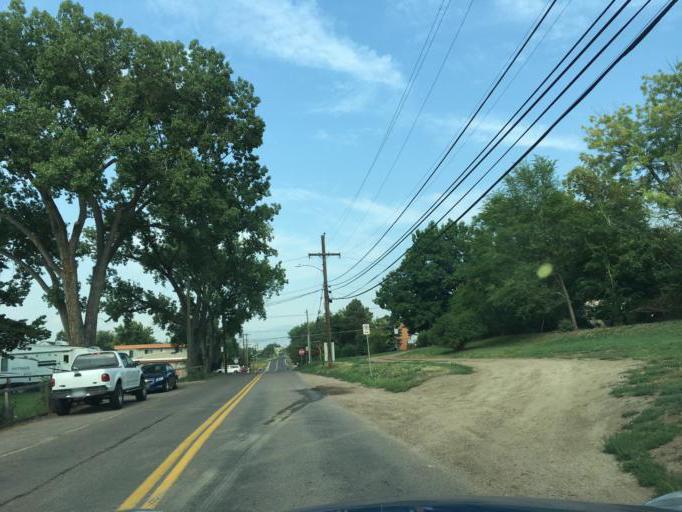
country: US
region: Colorado
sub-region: Jefferson County
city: Arvada
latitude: 39.8093
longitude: -105.0802
